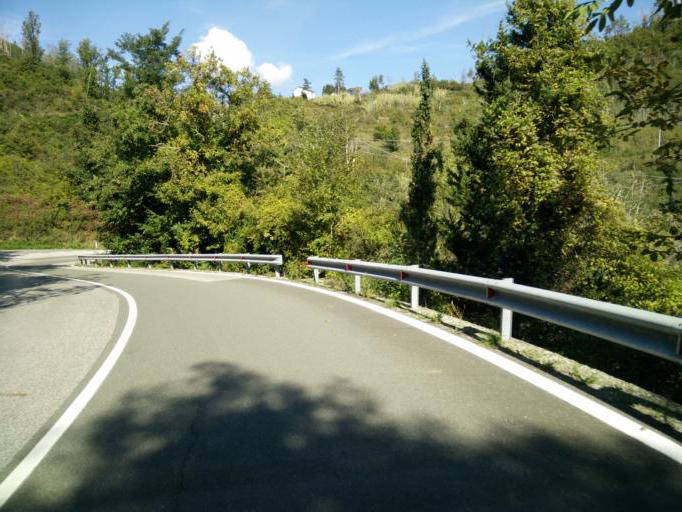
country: IT
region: Liguria
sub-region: Provincia di La Spezia
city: Carrodano
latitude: 44.2471
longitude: 9.6429
